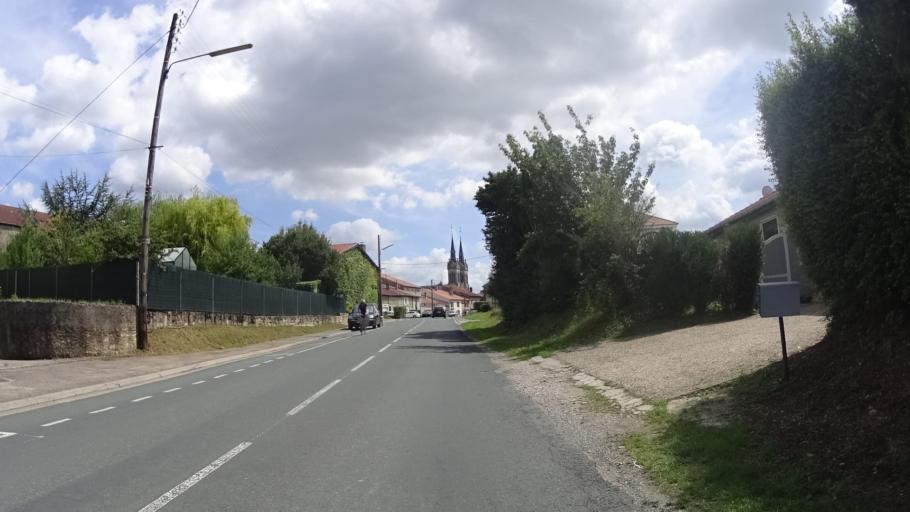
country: FR
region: Lorraine
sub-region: Departement de la Meuse
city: Euville
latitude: 48.7516
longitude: 5.6222
